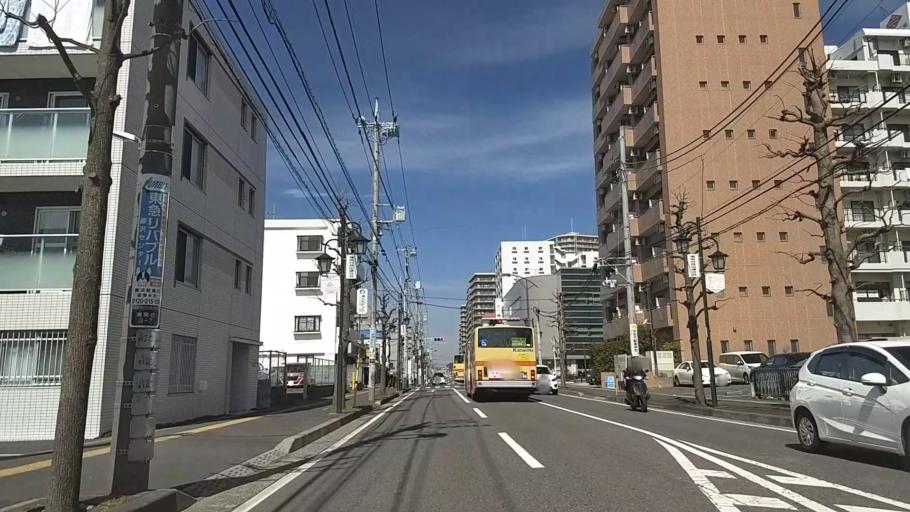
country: JP
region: Kanagawa
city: Fujisawa
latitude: 35.3949
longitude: 139.4634
